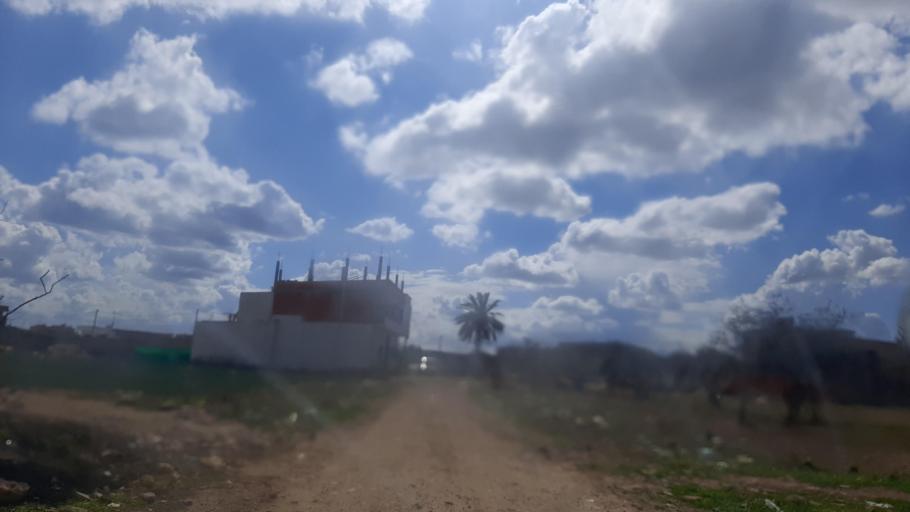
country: TN
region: Nabul
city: Korba
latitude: 36.5960
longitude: 10.8563
